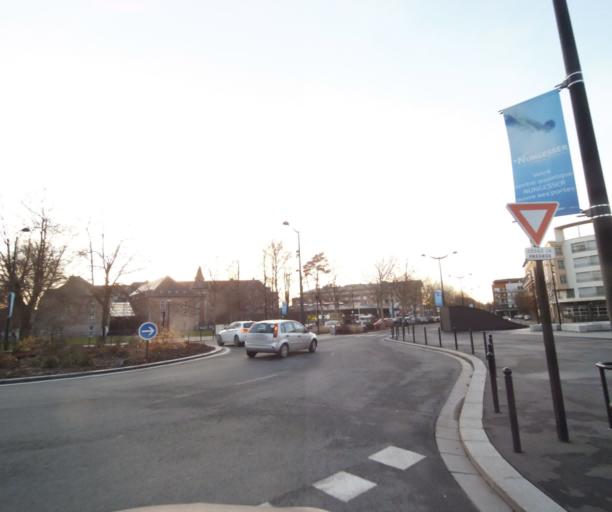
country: FR
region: Nord-Pas-de-Calais
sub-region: Departement du Nord
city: Valenciennes
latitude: 50.3640
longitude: 3.5294
